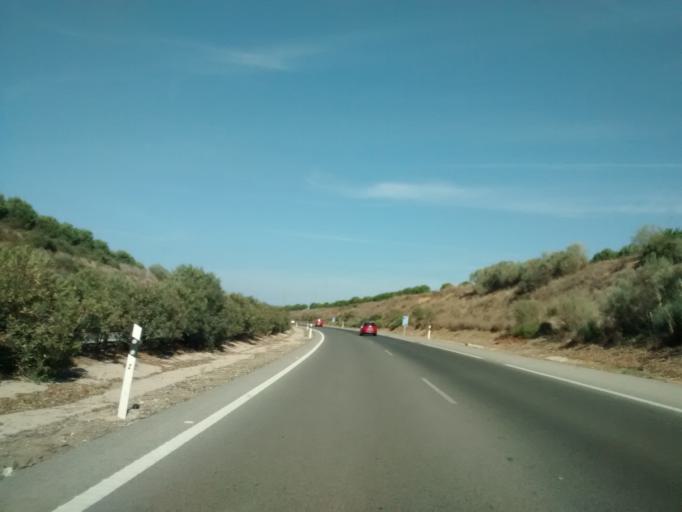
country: ES
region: Andalusia
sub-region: Provincia de Cadiz
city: Conil de la Frontera
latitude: 36.3442
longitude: -6.0531
